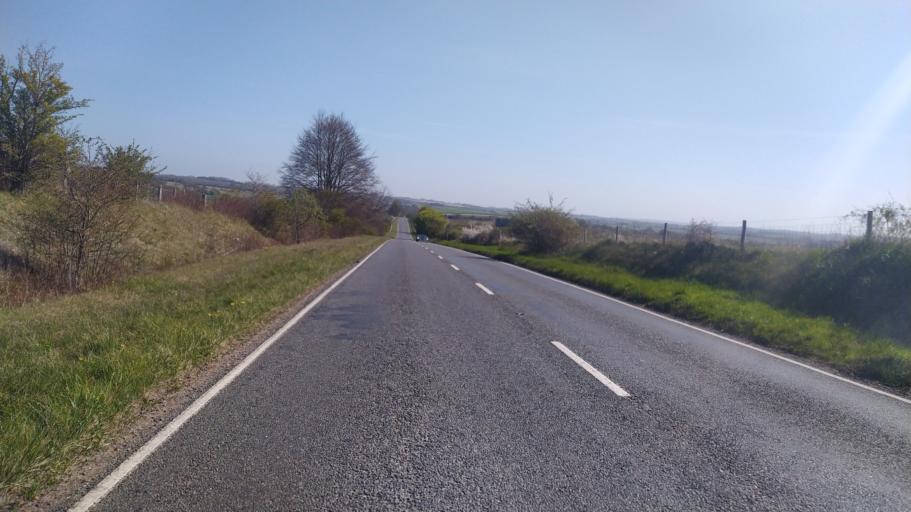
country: GB
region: England
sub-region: Wiltshire
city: Bower Chalke
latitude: 50.9814
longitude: -1.9471
